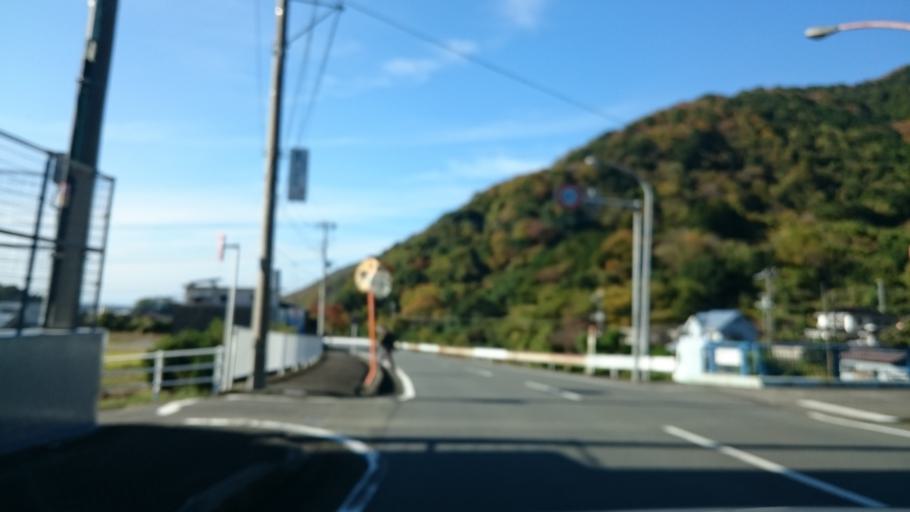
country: JP
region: Shizuoka
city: Heda
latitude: 34.9695
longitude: 138.7990
